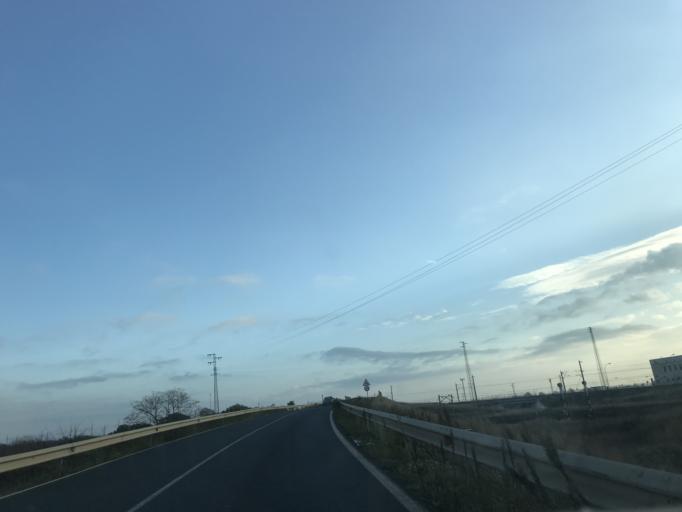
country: ES
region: Andalusia
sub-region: Provincia de Sevilla
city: Sevilla
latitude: 37.4177
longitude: -5.9536
